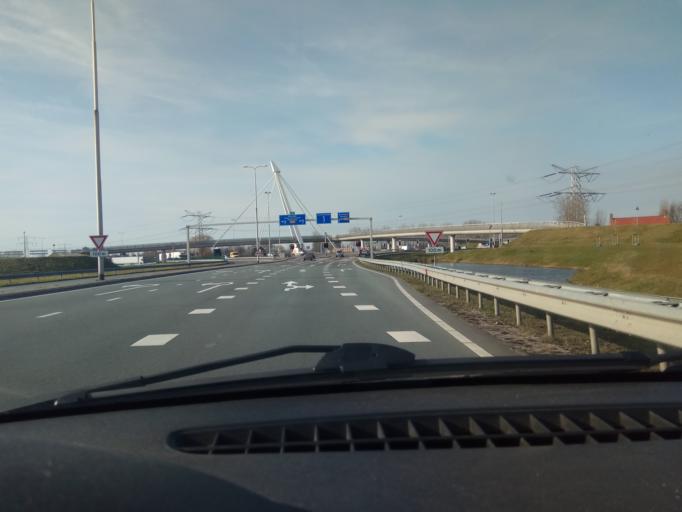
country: NL
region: South Holland
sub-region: Gemeente Westland
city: Naaldwijk
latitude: 51.9814
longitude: 4.2224
